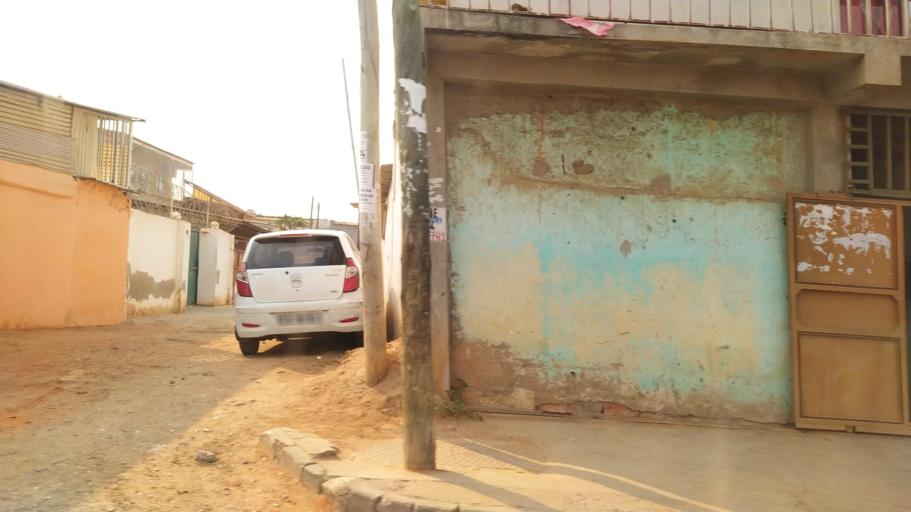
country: AO
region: Luanda
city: Luanda
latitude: -8.8959
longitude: 13.1978
